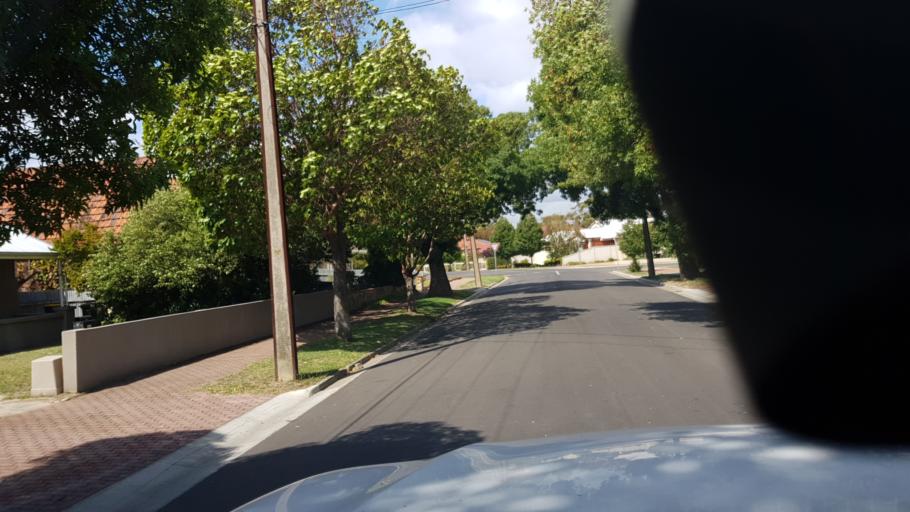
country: AU
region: South Australia
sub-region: Holdfast Bay
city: Glenelg East
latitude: -34.9771
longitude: 138.5326
